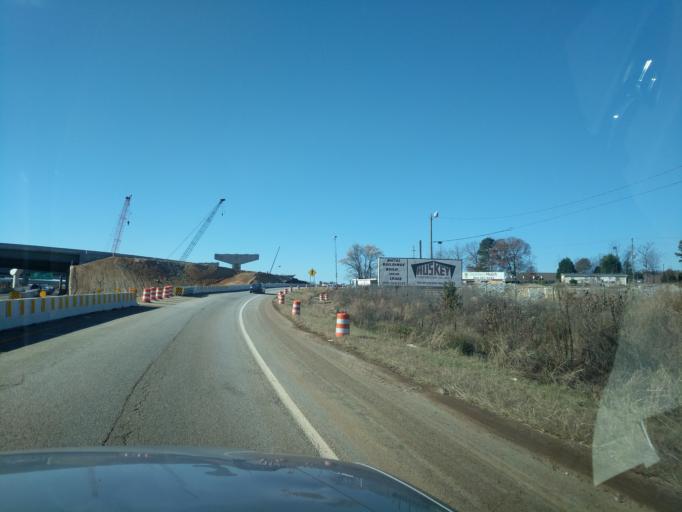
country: US
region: South Carolina
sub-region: Greenville County
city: Mauldin
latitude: 34.8357
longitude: -82.2931
